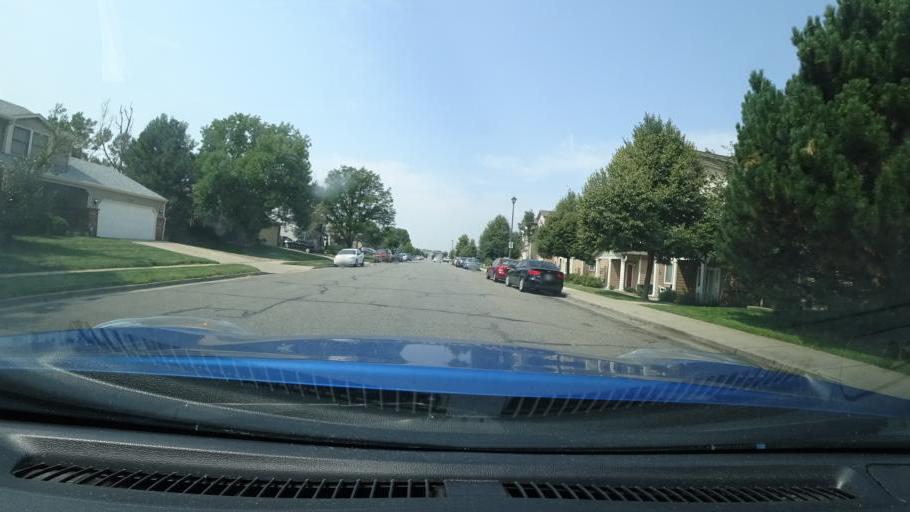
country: US
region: Colorado
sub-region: Adams County
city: Aurora
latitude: 39.7805
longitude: -104.7658
